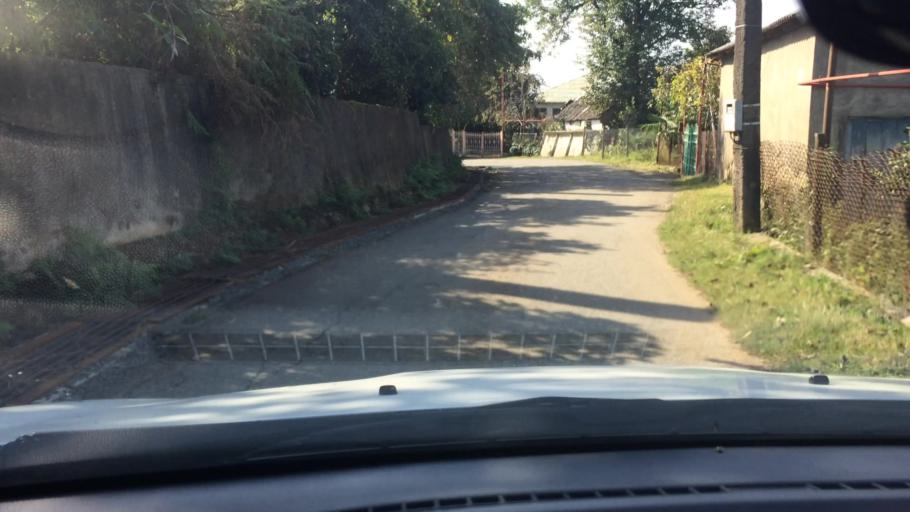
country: GE
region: Ajaria
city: Kobuleti
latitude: 41.8120
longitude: 41.8246
